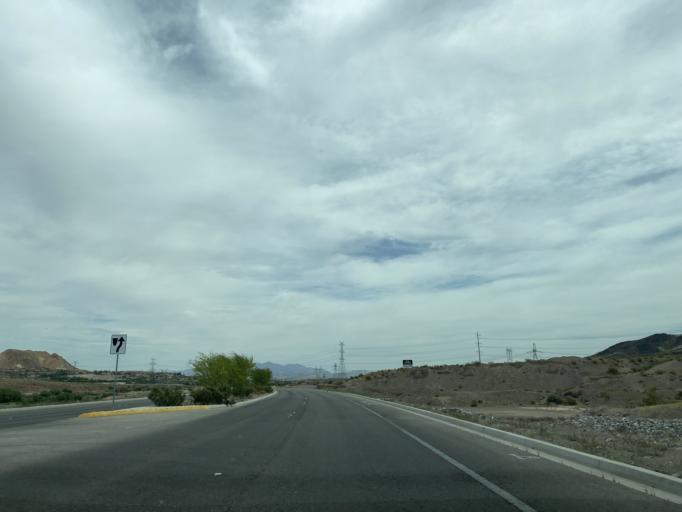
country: US
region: Nevada
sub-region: Clark County
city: Henderson
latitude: 36.0949
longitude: -114.9467
